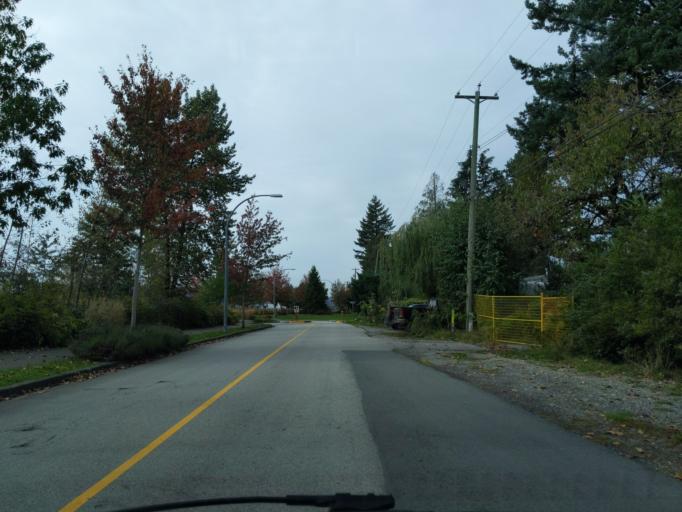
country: CA
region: British Columbia
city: Walnut Grove
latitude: 49.1815
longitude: -122.6590
